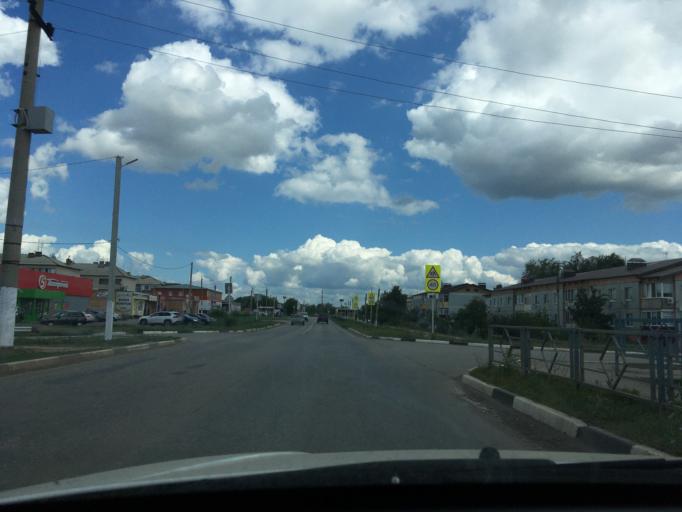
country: RU
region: Samara
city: Bezenchuk
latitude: 52.9929
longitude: 49.4373
